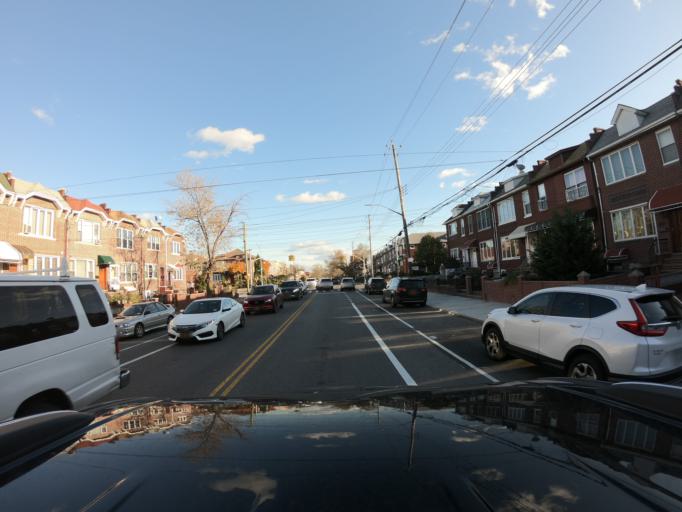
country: US
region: New York
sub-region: Kings County
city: Bensonhurst
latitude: 40.6232
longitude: -74.0123
